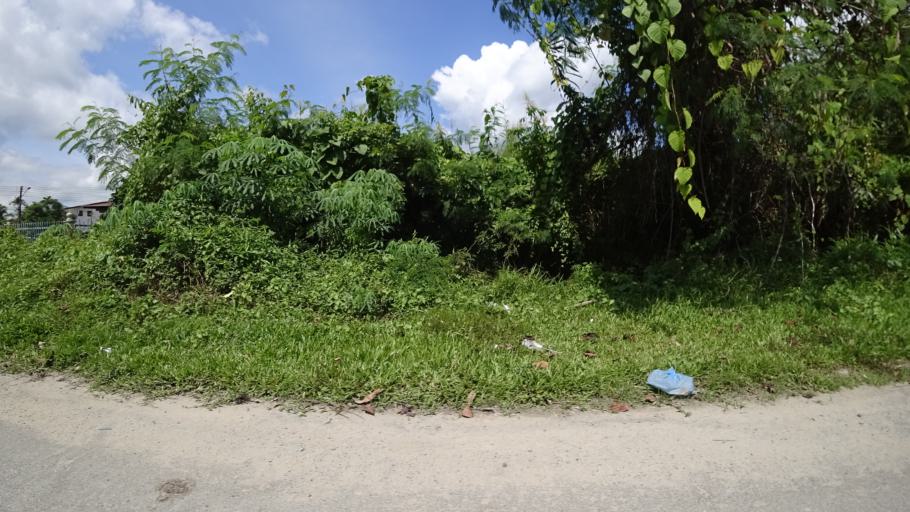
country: MY
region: Sarawak
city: Limbang
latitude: 4.7416
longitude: 114.9992
